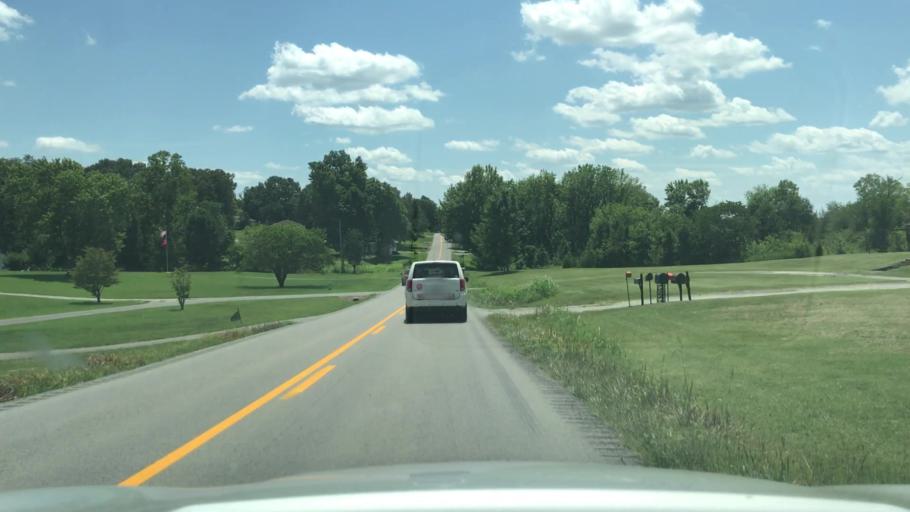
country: US
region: Kentucky
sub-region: Christian County
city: Hopkinsville
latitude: 36.9044
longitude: -87.4469
